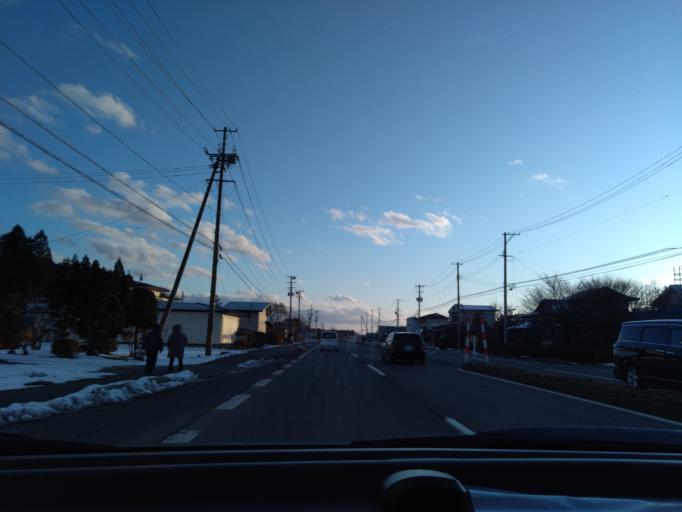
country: JP
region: Iwate
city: Hanamaki
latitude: 39.5265
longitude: 141.1628
